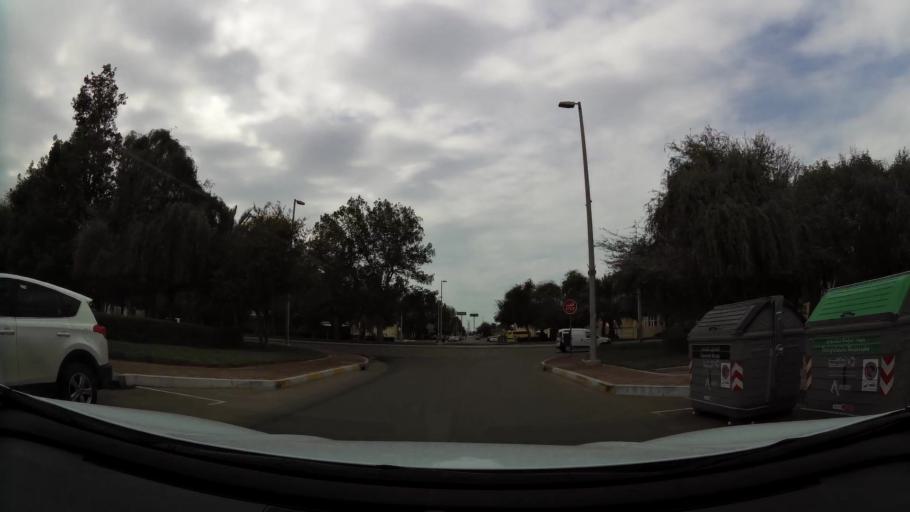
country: AE
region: Abu Dhabi
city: Abu Dhabi
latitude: 24.4276
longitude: 54.4118
